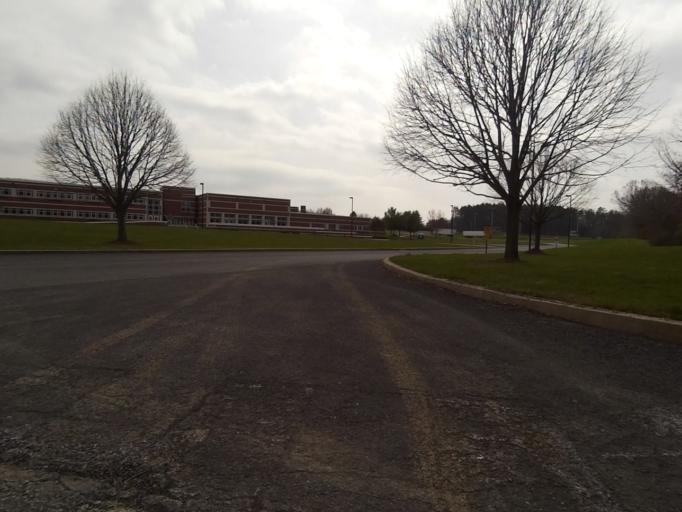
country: US
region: Pennsylvania
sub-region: Centre County
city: Boalsburg
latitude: 40.7881
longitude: -77.8068
